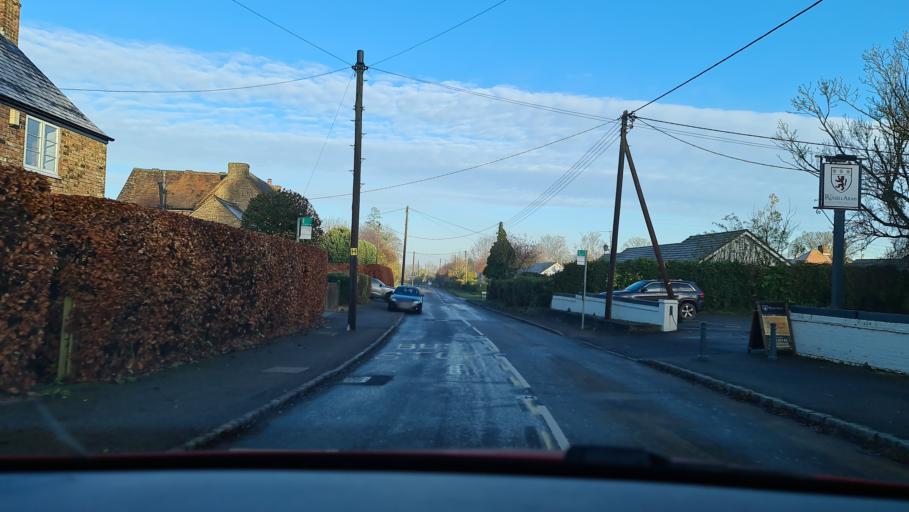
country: GB
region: England
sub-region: Buckinghamshire
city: Wendover
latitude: 51.7558
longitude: -0.7806
